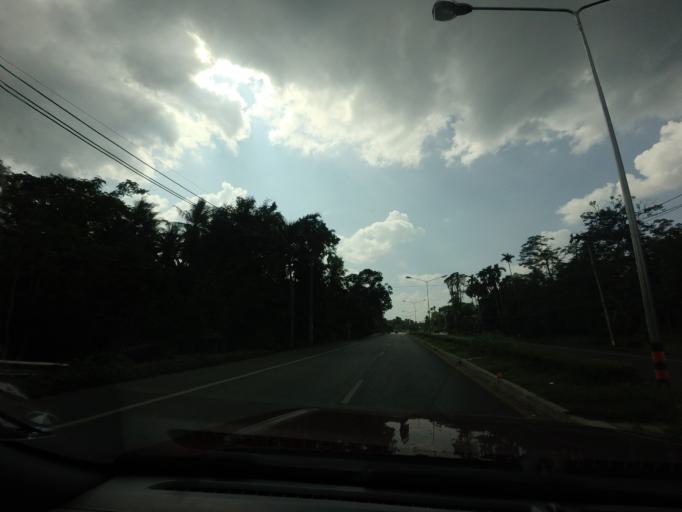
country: TH
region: Yala
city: Krong Pi Nang
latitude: 6.4716
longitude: 101.2670
